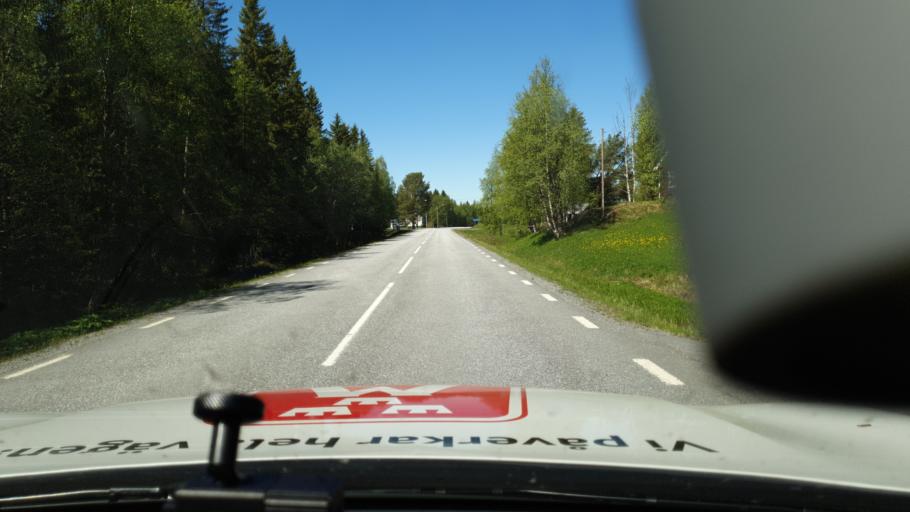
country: SE
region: Vaesterbotten
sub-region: Storumans Kommun
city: Storuman
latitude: 65.1998
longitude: 17.0028
